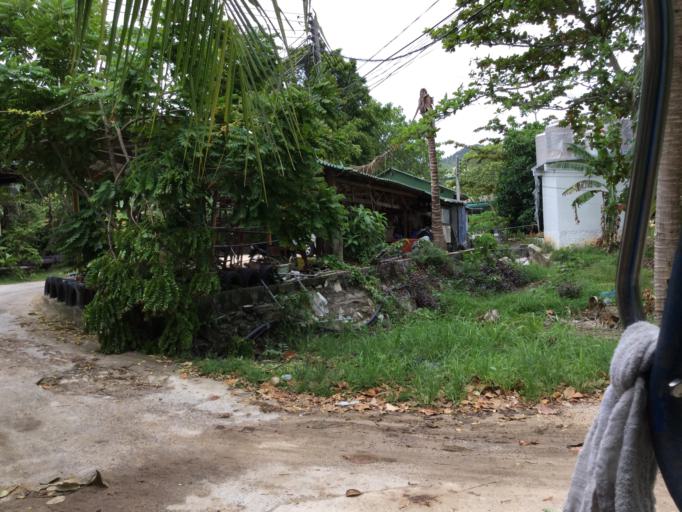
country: TH
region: Nakhon Si Thammarat
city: Ko Pha Ngan
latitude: 9.7707
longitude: 100.0563
